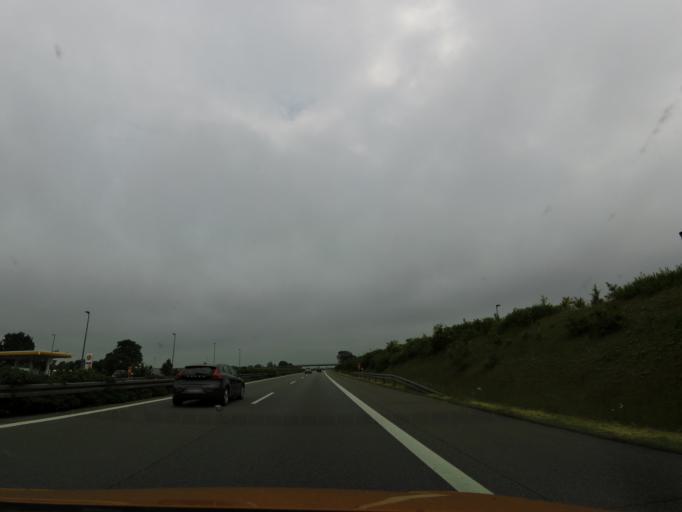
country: DE
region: Mecklenburg-Vorpommern
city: Selmsdorf
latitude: 53.8152
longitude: 10.8773
